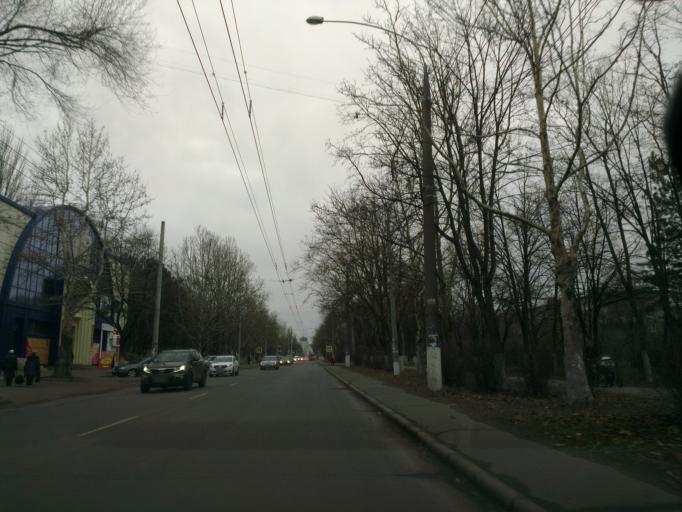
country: MD
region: Chisinau
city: Chisinau
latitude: 46.9796
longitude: 28.8536
